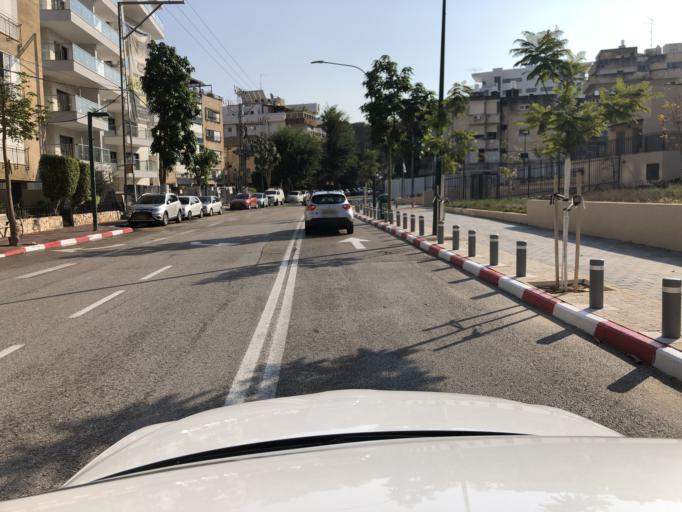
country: IL
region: Tel Aviv
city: Ramat Gan
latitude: 32.0898
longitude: 34.8203
